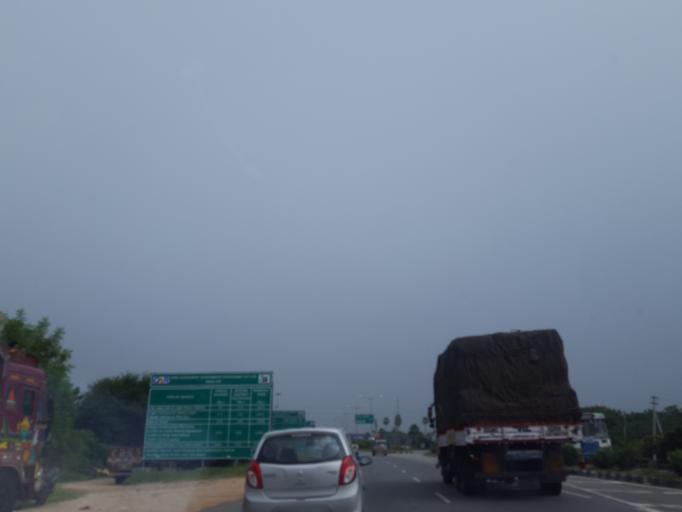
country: IN
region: Telangana
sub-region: Nalgonda
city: Gudur
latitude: 17.2346
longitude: 78.9545
